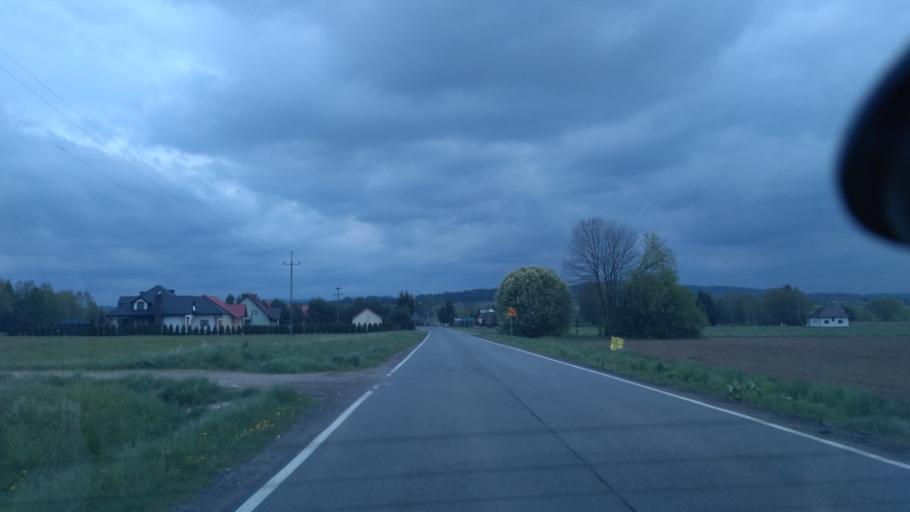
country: PL
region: Subcarpathian Voivodeship
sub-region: Powiat brzozowski
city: Jasionow
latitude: 49.6451
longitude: 21.9725
